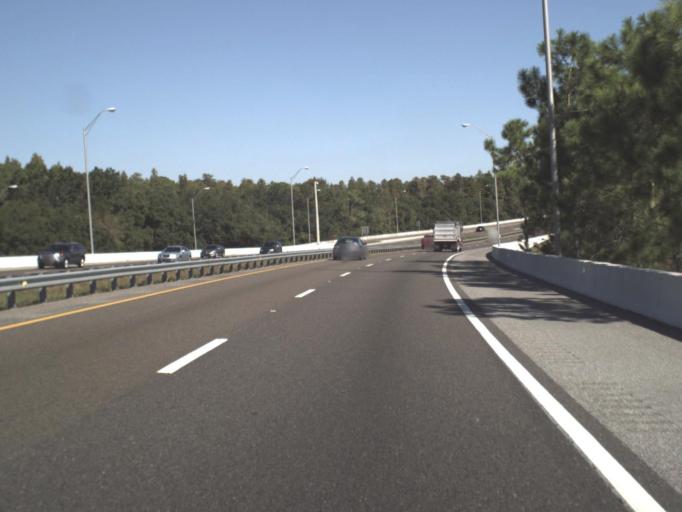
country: US
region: Florida
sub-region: Hillsborough County
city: Citrus Park
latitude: 28.0797
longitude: -82.5619
